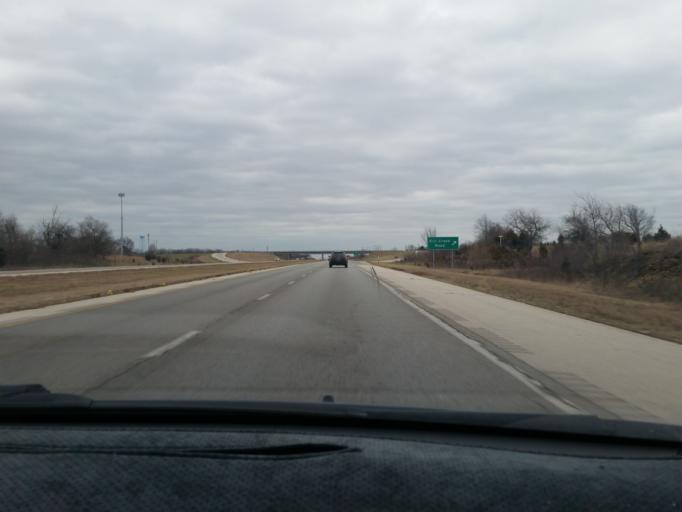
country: US
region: Kansas
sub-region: Johnson County
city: De Soto
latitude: 38.9600
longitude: -94.9621
